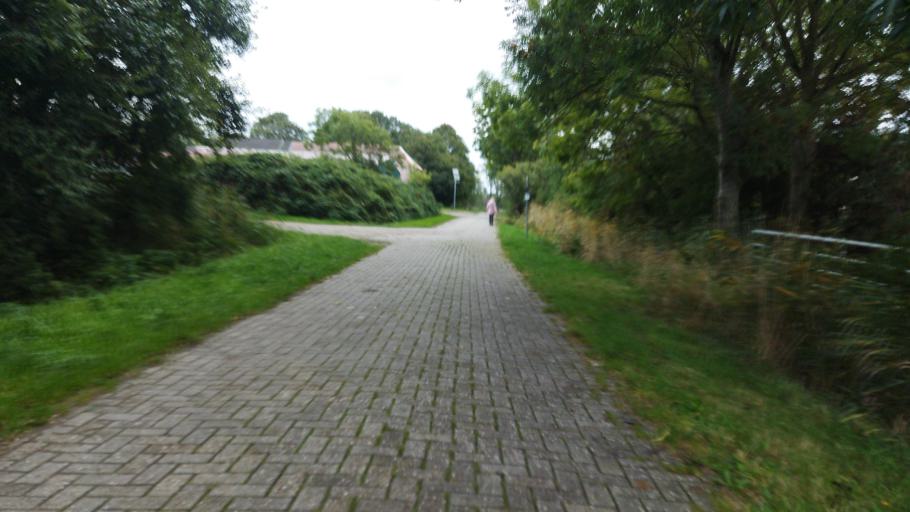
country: DE
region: Lower Saxony
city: Hinte
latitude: 53.3983
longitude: 7.1989
